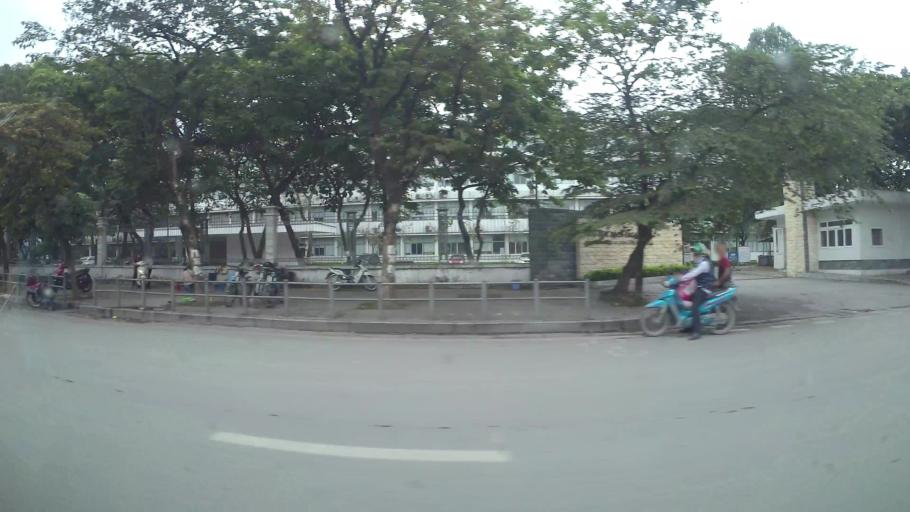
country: VN
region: Ha Noi
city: Hai BaTrung
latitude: 21.0075
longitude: 105.8429
